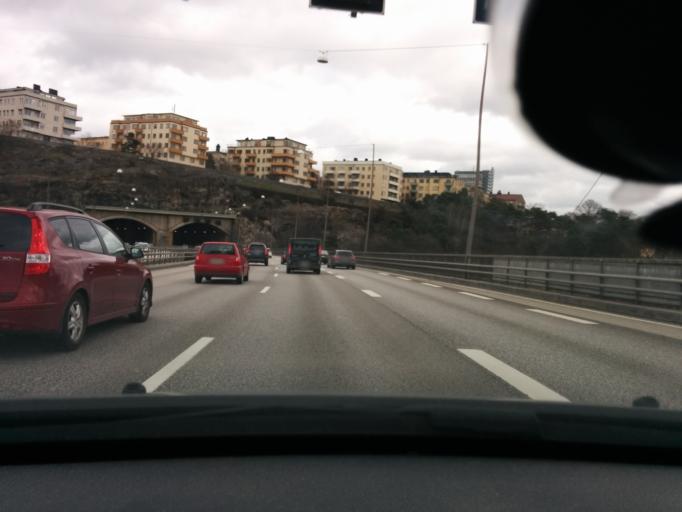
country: SE
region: Stockholm
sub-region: Solna Kommun
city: Solna
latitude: 59.3261
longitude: 18.0059
